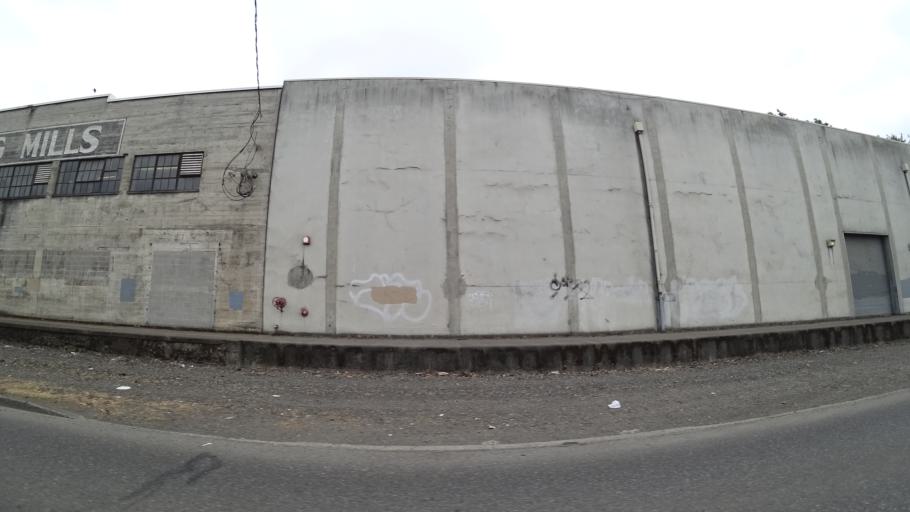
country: US
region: Washington
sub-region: Clark County
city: Vancouver
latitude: 45.5860
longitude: -122.6881
